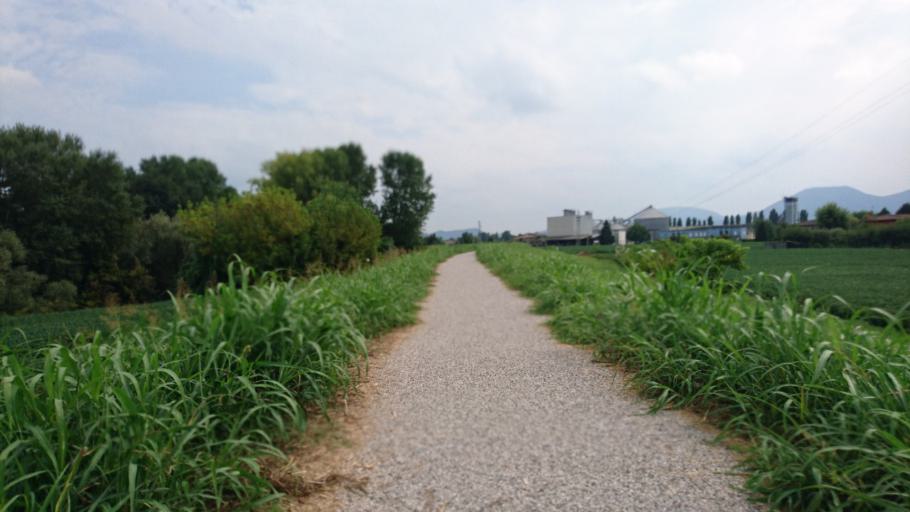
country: IT
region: Veneto
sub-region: Provincia di Padova
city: Cervarese Santa Croce
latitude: 45.4257
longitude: 11.6945
